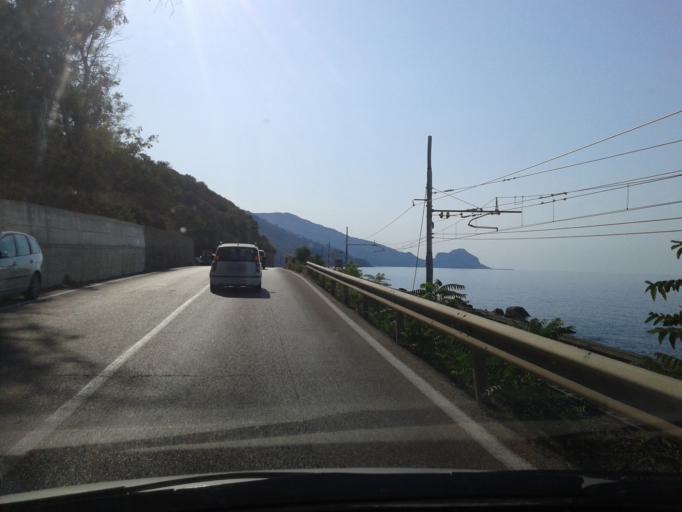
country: IT
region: Sicily
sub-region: Palermo
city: Pollina
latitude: 38.0166
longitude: 14.1254
